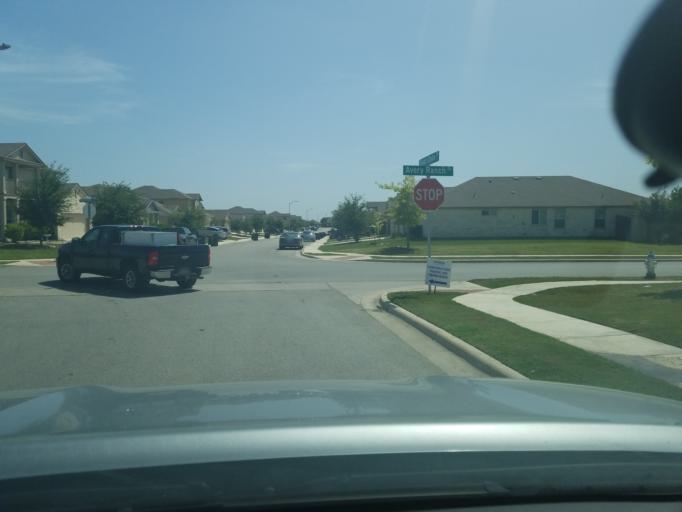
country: US
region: Texas
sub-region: Guadalupe County
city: Lake Dunlap
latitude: 29.6712
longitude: -98.0377
